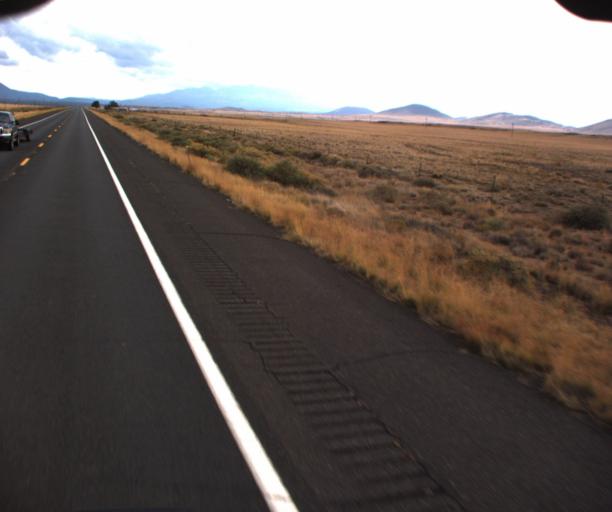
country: US
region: Arizona
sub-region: Coconino County
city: Flagstaff
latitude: 35.6010
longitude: -111.5258
